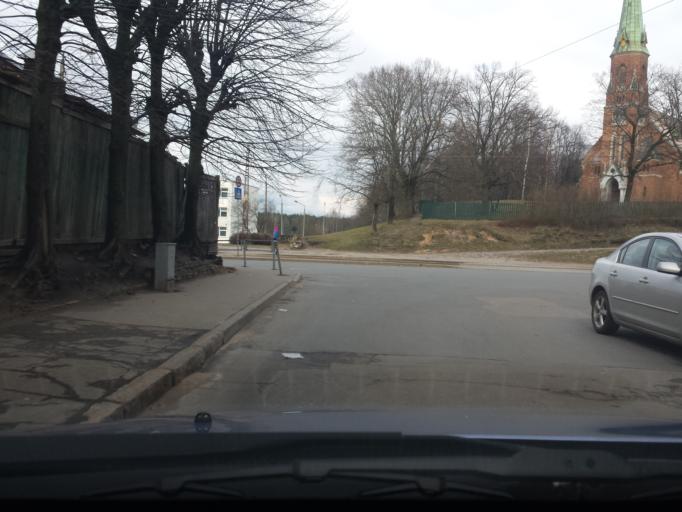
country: LV
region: Riga
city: Riga
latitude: 56.9980
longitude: 24.1230
